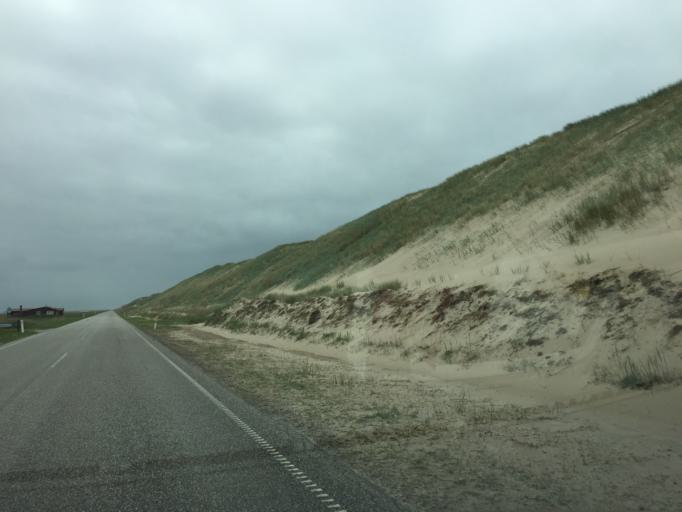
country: DK
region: Central Jutland
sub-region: Lemvig Kommune
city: Harboore
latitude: 56.4418
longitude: 8.1248
